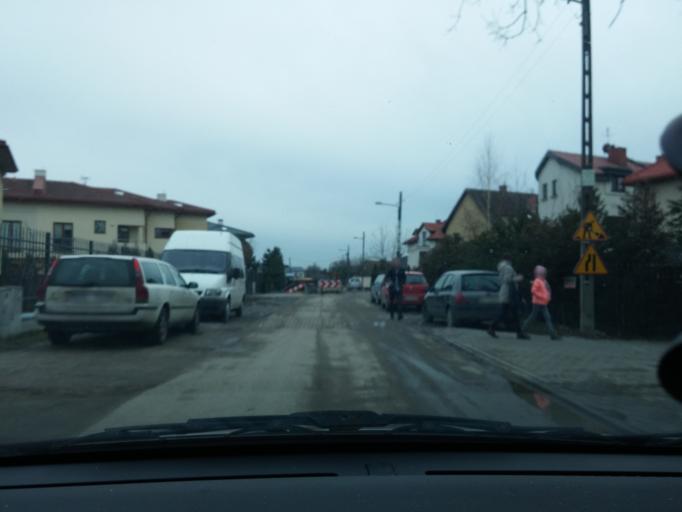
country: PL
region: Masovian Voivodeship
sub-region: Warszawa
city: Wawer
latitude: 52.1975
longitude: 21.1273
